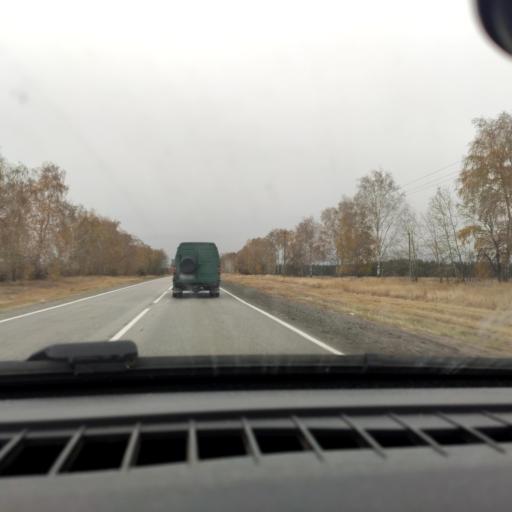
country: RU
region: Voronezj
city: Uryv-Pokrovka
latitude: 51.0608
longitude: 38.9921
